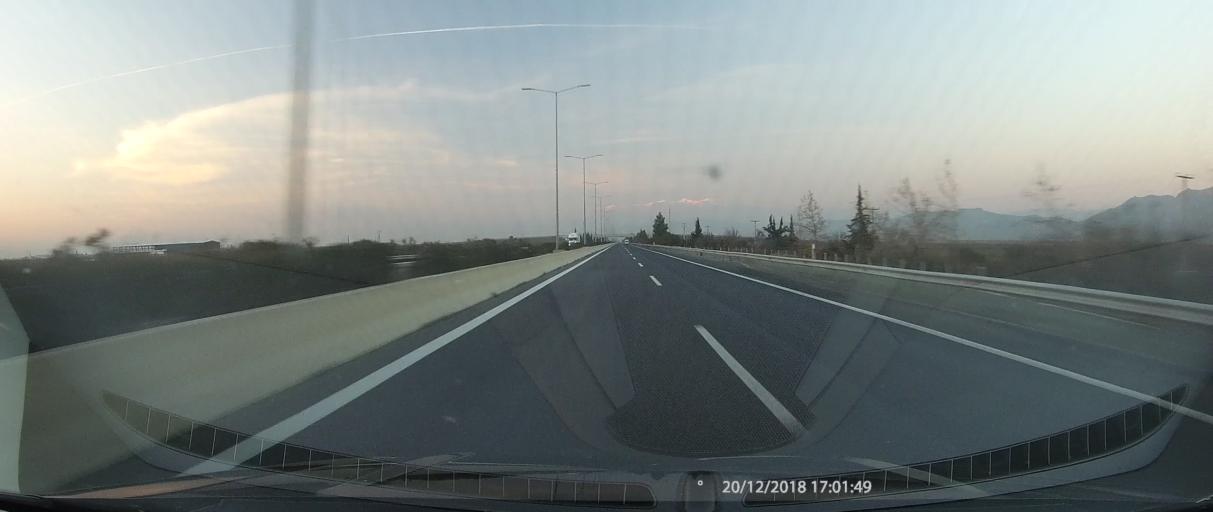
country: GR
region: Thessaly
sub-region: Nomos Larisis
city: Platykampos
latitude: 39.6631
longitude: 22.5038
